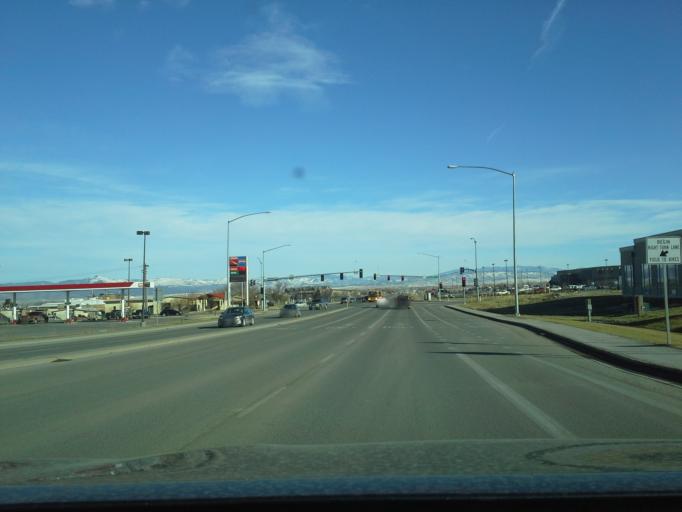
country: US
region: Montana
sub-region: Lewis and Clark County
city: Helena
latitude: 46.6166
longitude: -112.0073
